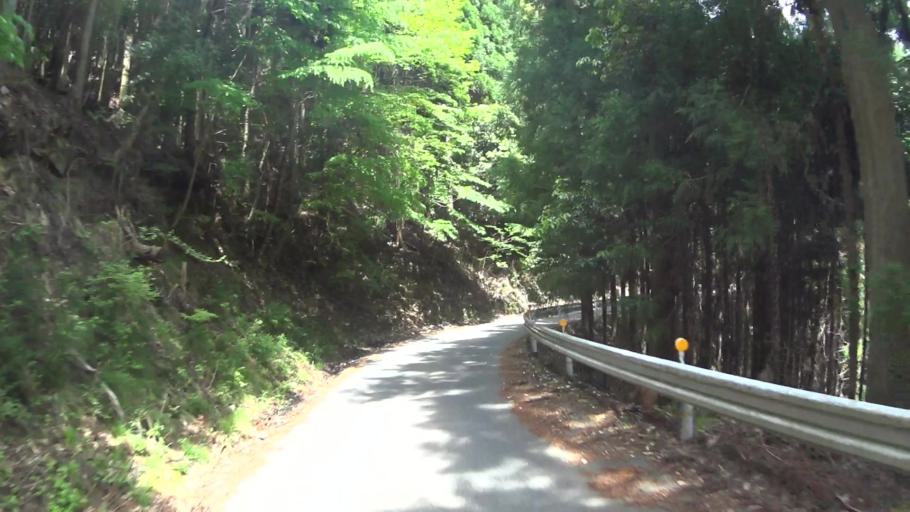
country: JP
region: Kyoto
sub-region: Kyoto-shi
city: Kamigyo-ku
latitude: 35.1151
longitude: 135.7119
